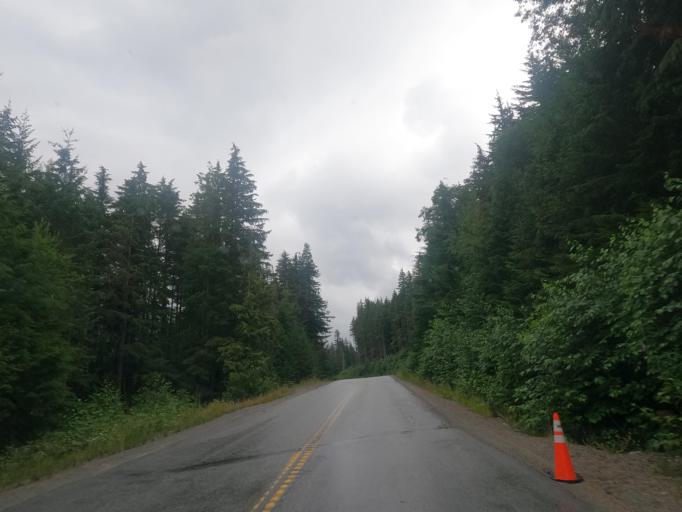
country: CA
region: British Columbia
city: Pemberton
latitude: 50.3198
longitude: -122.5625
